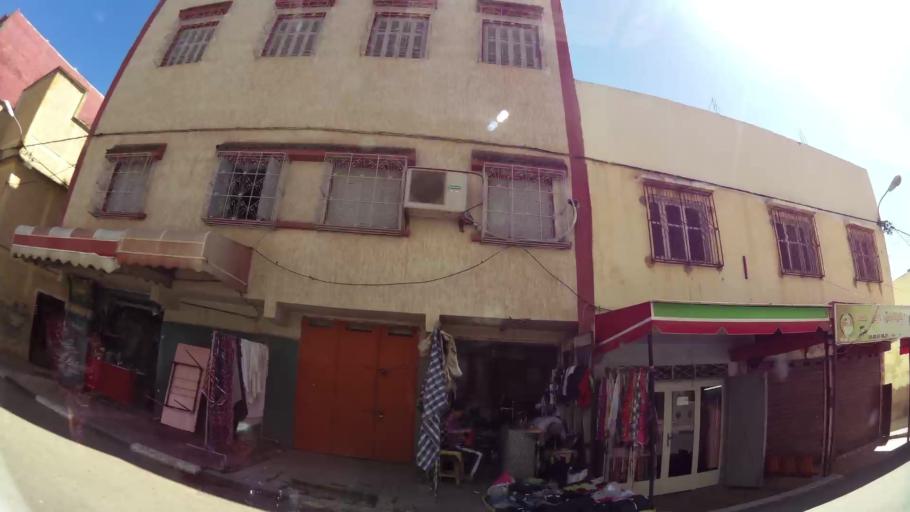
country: MA
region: Meknes-Tafilalet
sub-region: Meknes
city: Meknes
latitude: 33.8844
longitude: -5.5790
